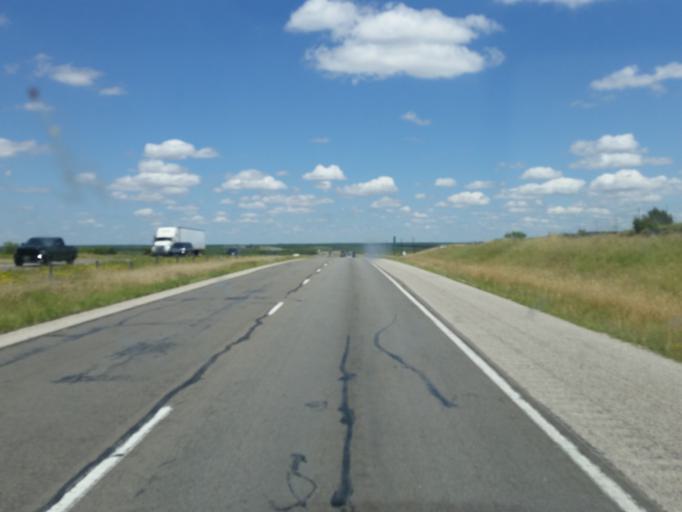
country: US
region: Texas
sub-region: Nolan County
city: Sweetwater
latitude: 32.4955
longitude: -100.2647
